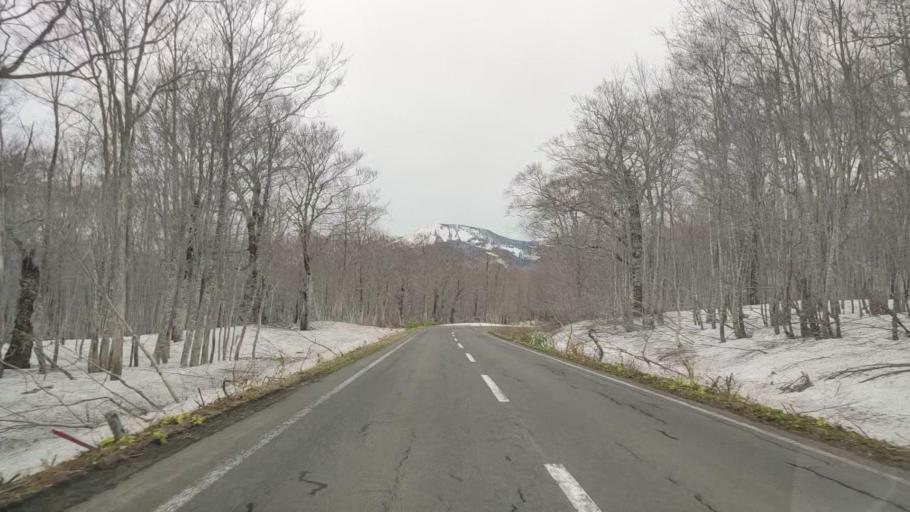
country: JP
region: Aomori
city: Aomori Shi
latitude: 40.6351
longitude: 140.9298
